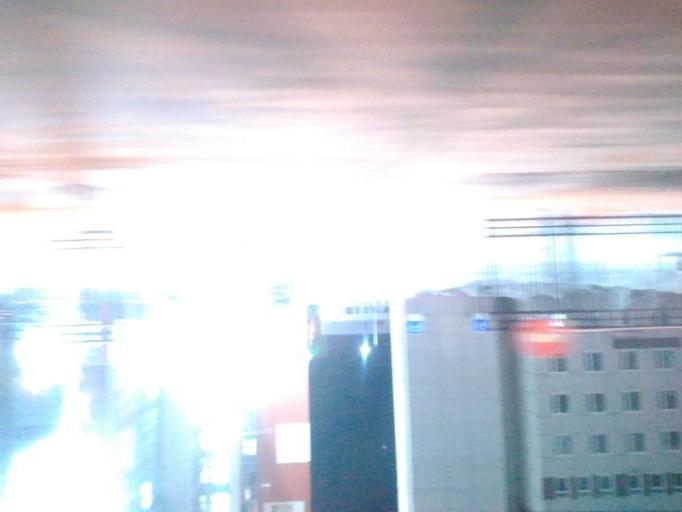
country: RU
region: Ulyanovsk
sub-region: Ulyanovskiy Rayon
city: Ulyanovsk
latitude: 54.3272
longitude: 48.4034
